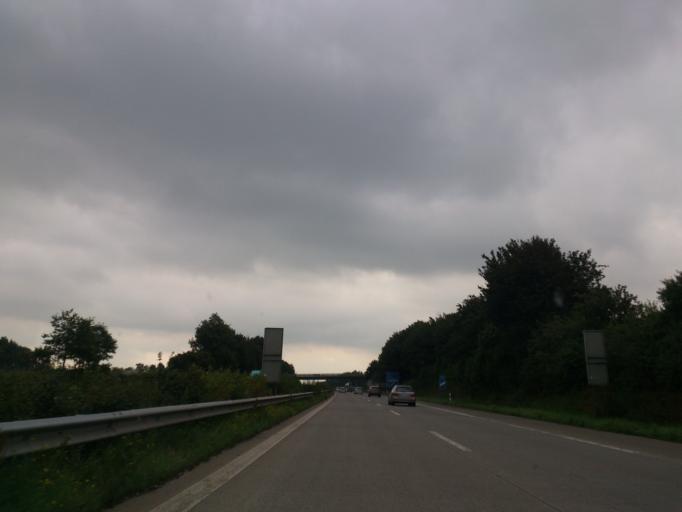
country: DE
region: Schleswig-Holstein
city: Rethwisch
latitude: 53.8455
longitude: 9.5951
